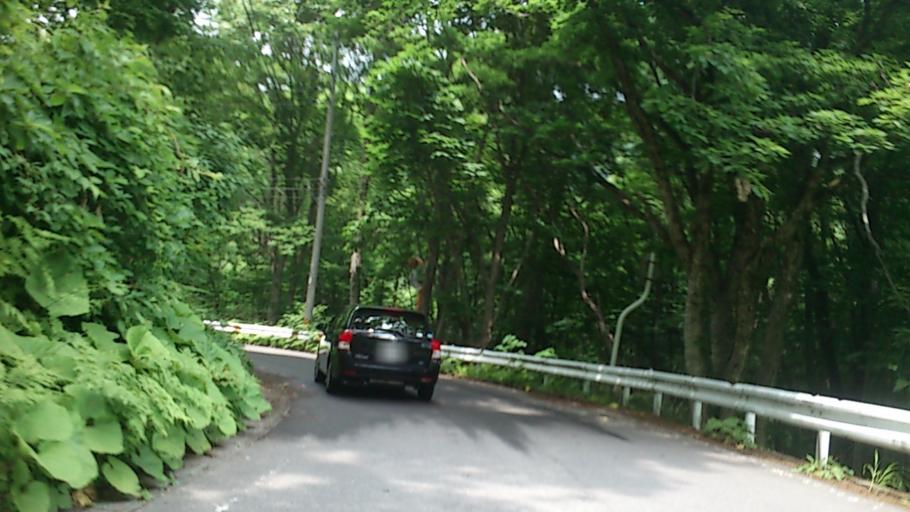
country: JP
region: Aomori
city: Hirosaki
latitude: 40.5171
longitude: 140.1934
